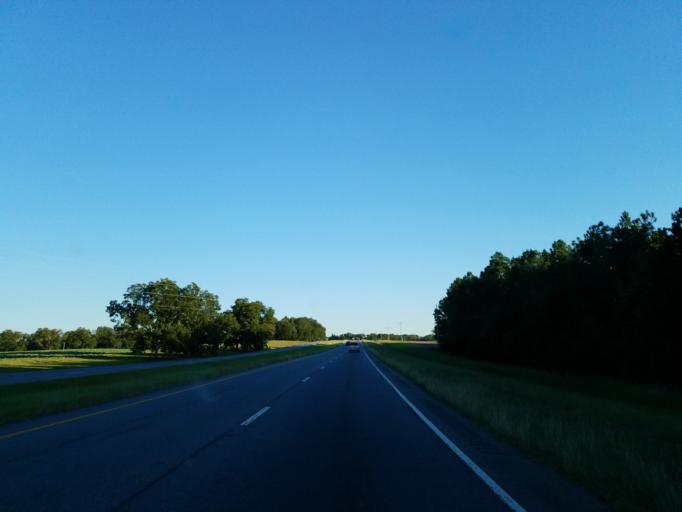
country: US
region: Georgia
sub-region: Worth County
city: Sylvester
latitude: 31.4943
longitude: -83.7078
